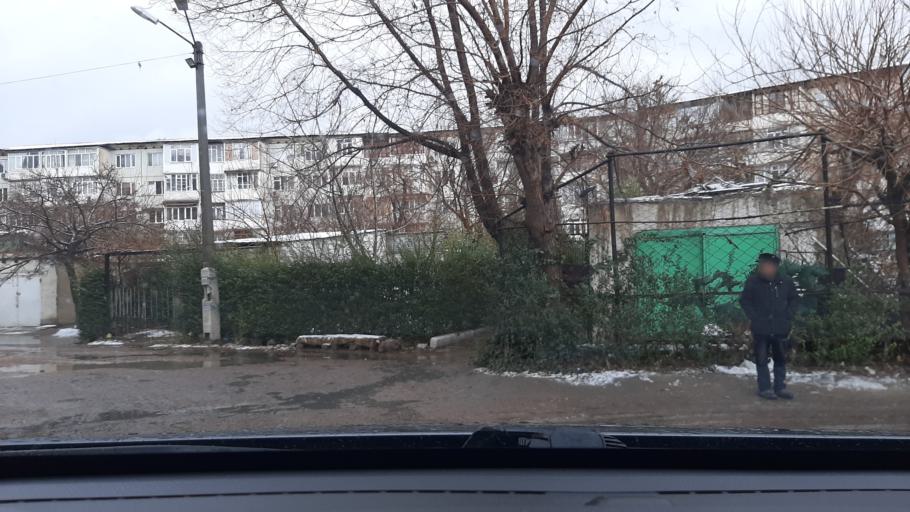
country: TJ
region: Viloyati Sughd
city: Khujand
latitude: 40.3004
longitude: 69.6082
